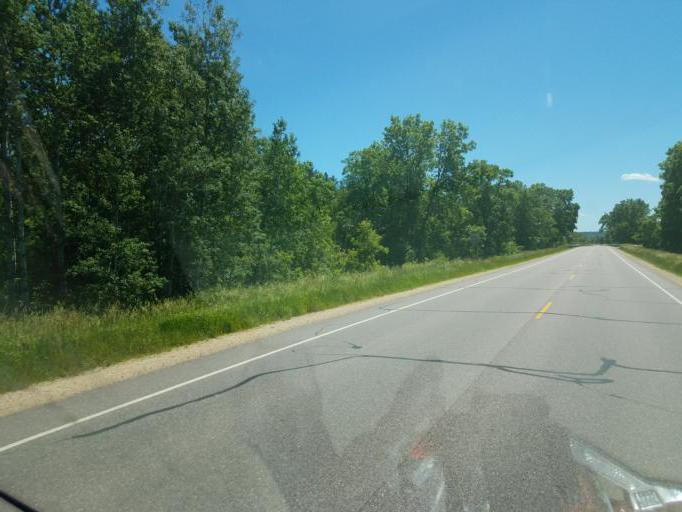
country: US
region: Wisconsin
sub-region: Juneau County
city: Elroy
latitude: 43.7078
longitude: -90.2662
